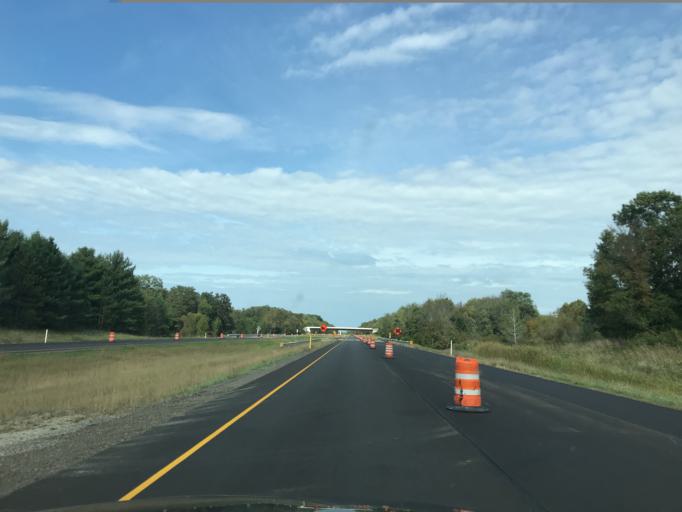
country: US
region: Ohio
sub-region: Ashtabula County
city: Jefferson
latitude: 41.7811
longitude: -80.7320
